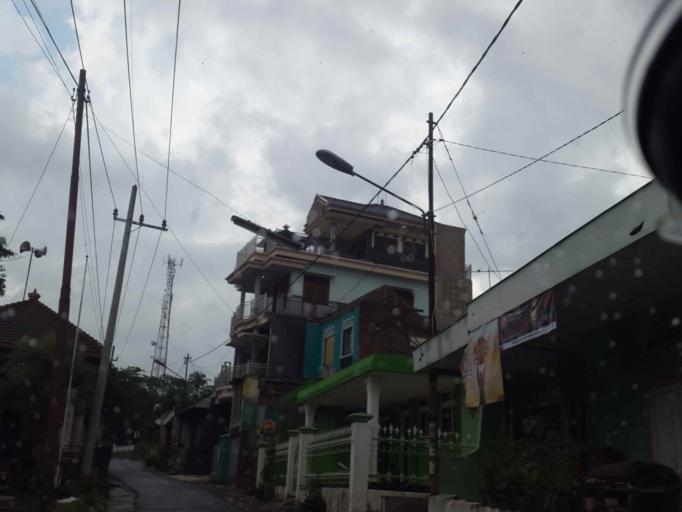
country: ID
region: East Java
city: Batu
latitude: -7.8648
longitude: 112.5590
